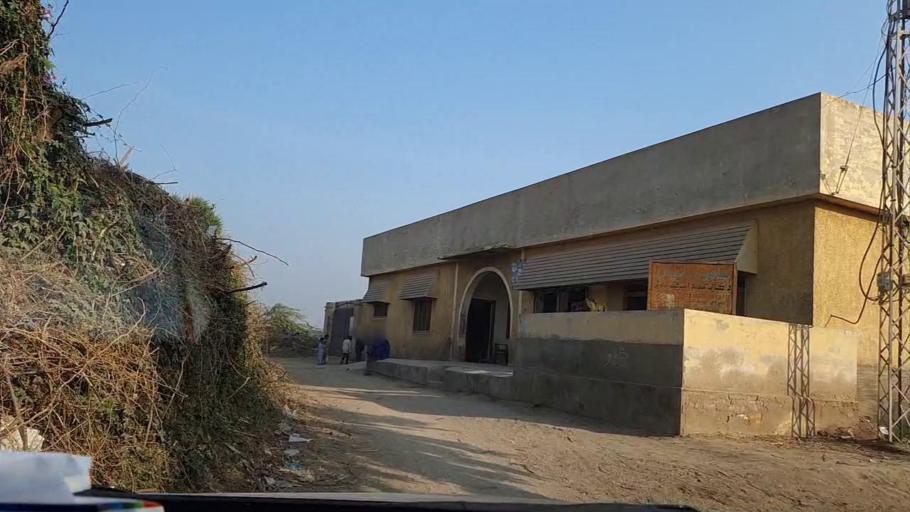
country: PK
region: Sindh
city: Tando Ghulam Ali
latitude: 25.2096
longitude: 68.9003
